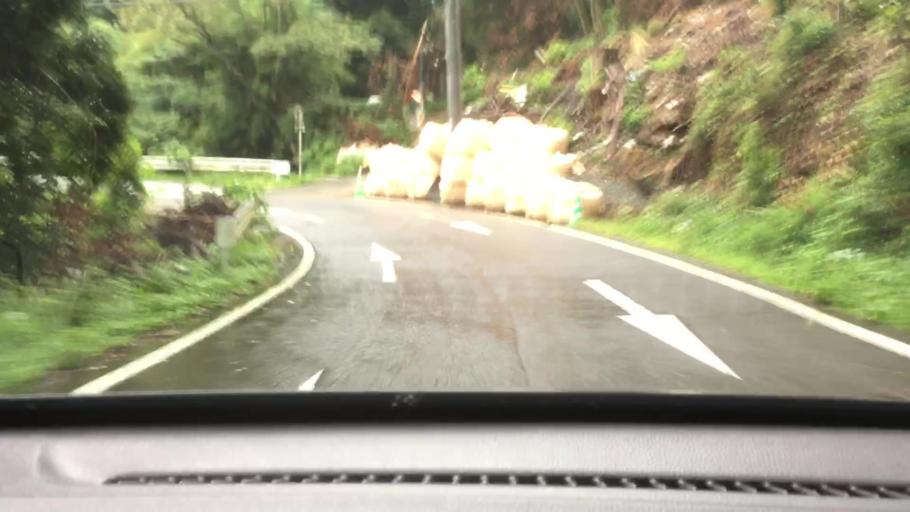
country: JP
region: Nagasaki
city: Togitsu
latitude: 32.8729
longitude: 129.7627
